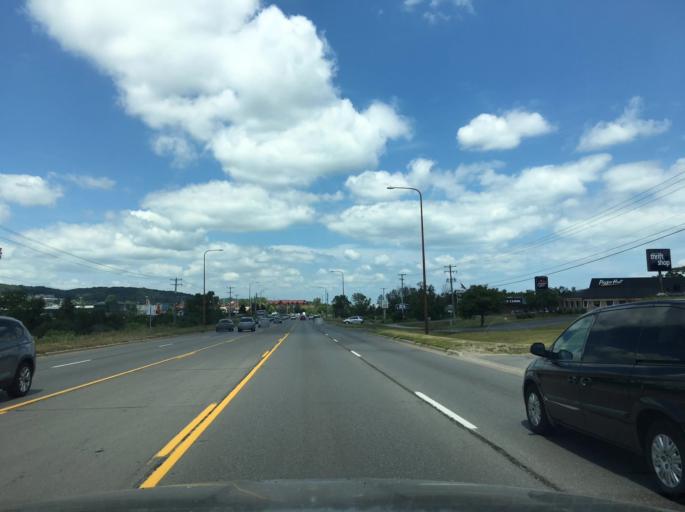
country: US
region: Michigan
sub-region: Grand Traverse County
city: Traverse City
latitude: 44.7298
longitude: -85.6461
